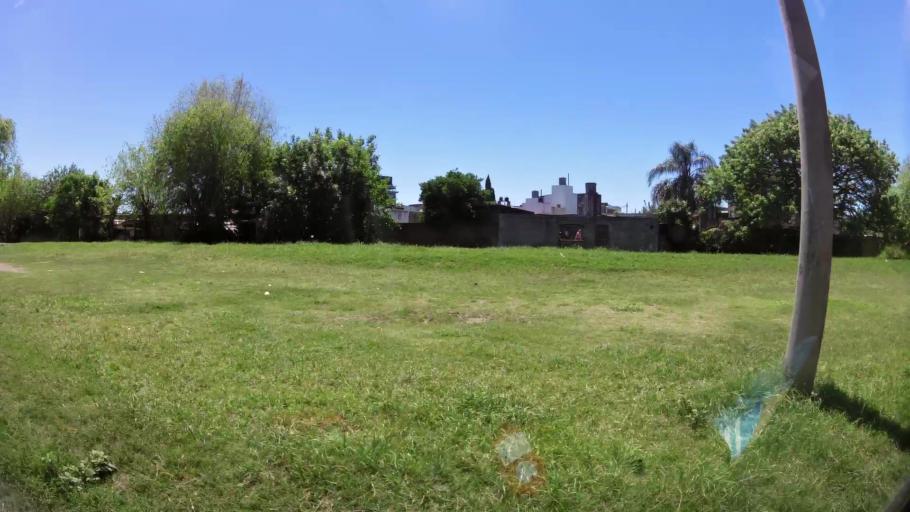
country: AR
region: Santa Fe
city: Santa Fe de la Vera Cruz
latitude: -31.6258
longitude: -60.7082
